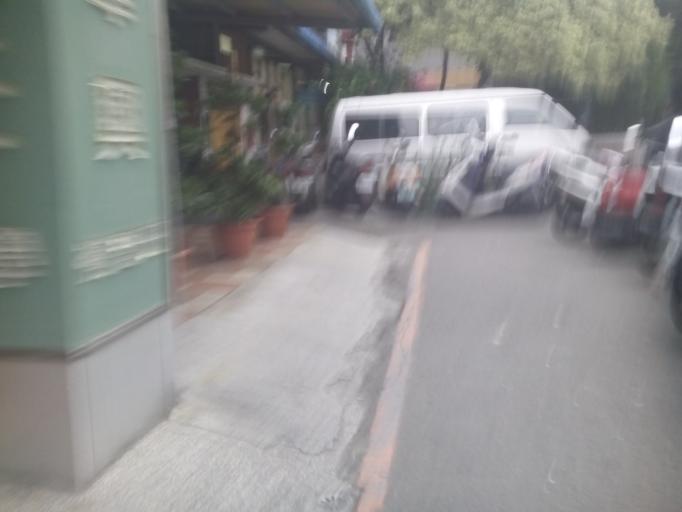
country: TW
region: Taipei
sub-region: Taipei
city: Banqiao
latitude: 25.0193
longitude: 121.4665
